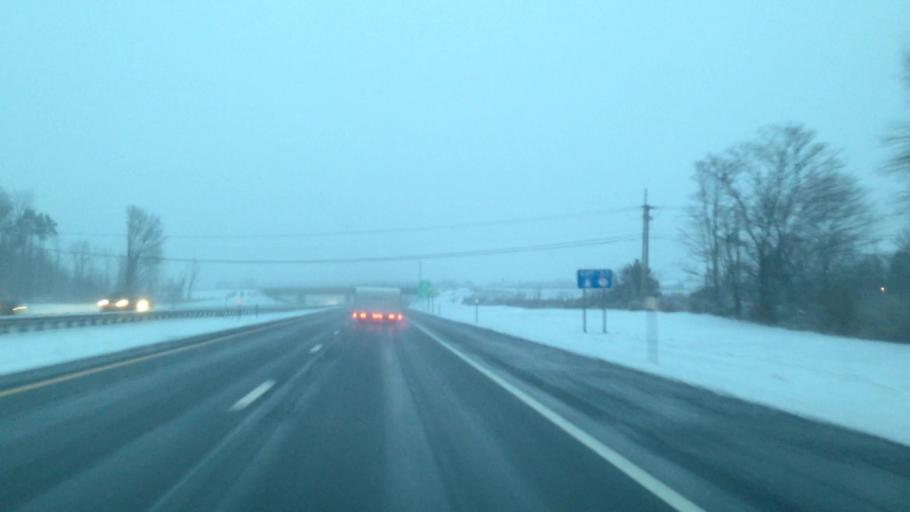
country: US
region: New York
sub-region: Oneida County
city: Sherrill
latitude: 43.1245
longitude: -75.5938
